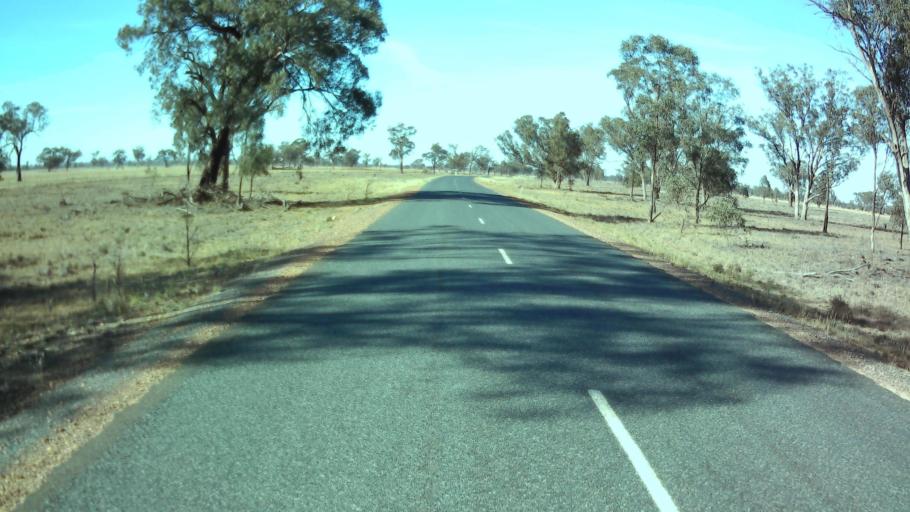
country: AU
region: New South Wales
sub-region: Weddin
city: Grenfell
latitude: -34.0680
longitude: 147.9057
